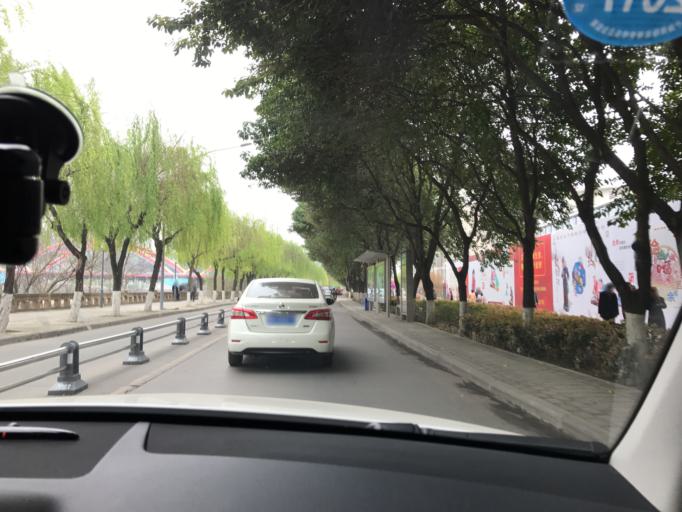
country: CN
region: Sichuan
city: Mianyang
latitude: 31.4550
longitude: 104.7200
